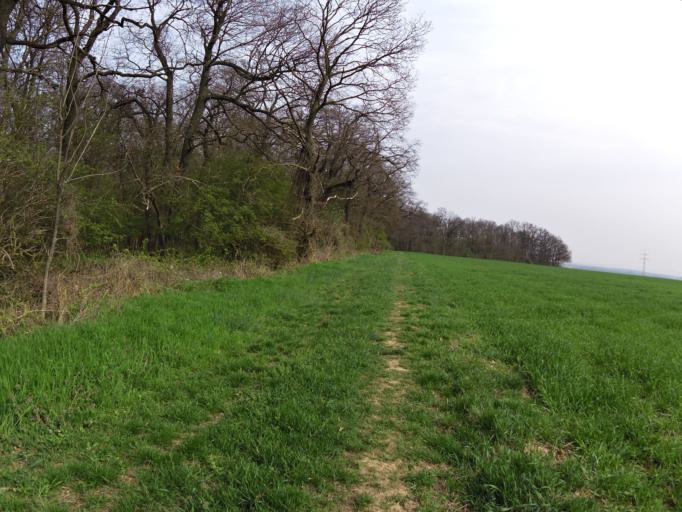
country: DE
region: Bavaria
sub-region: Regierungsbezirk Unterfranken
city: Rottendorf
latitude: 49.7758
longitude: 10.0395
